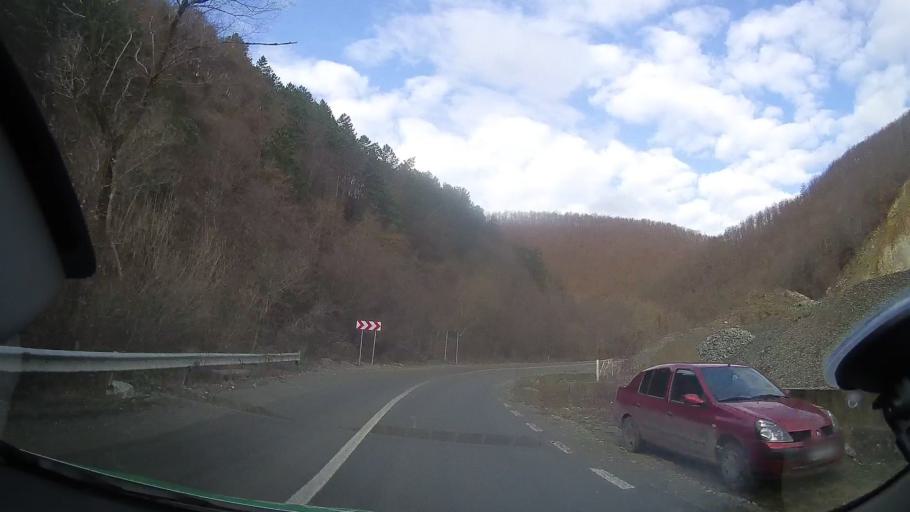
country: RO
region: Cluj
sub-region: Comuna Baisoara
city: Baisoara
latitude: 46.5858
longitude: 23.4486
